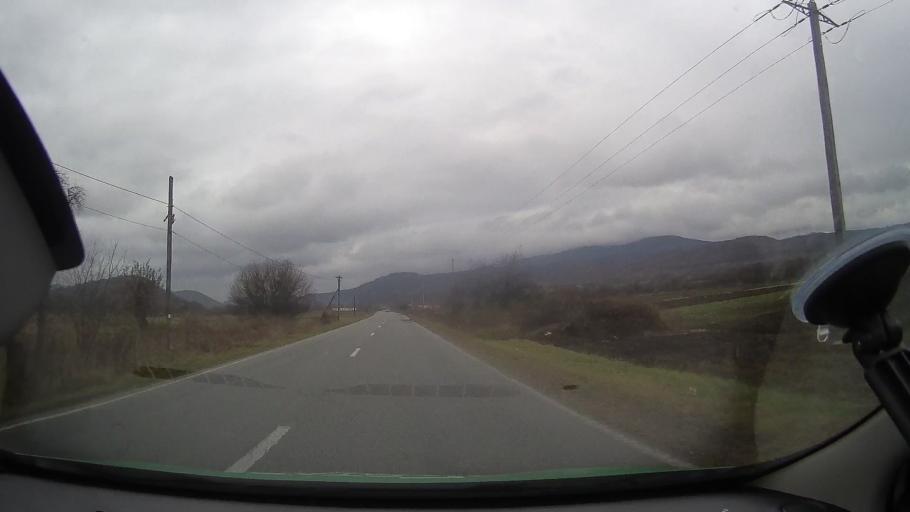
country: RO
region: Arad
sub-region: Comuna Buteni
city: Buteni
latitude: 46.3169
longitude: 22.1356
